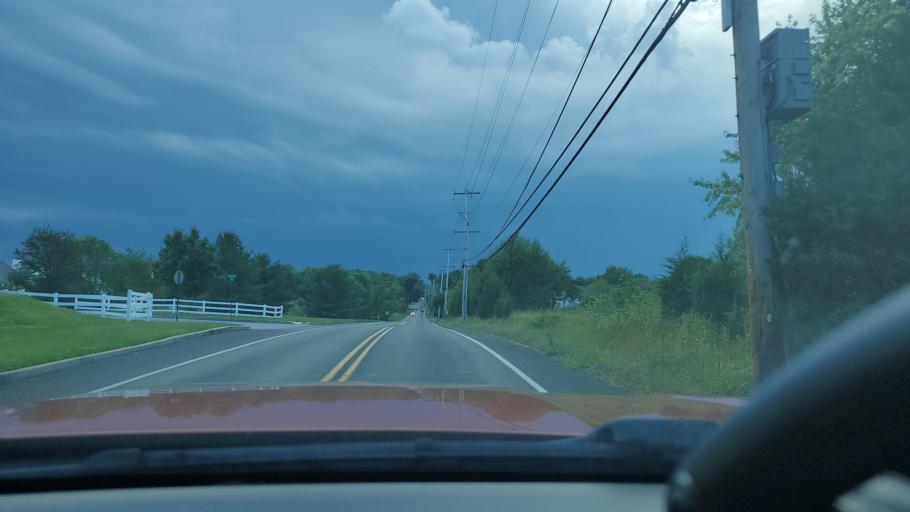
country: US
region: Pennsylvania
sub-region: Montgomery County
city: Limerick
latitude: 40.2365
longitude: -75.5107
